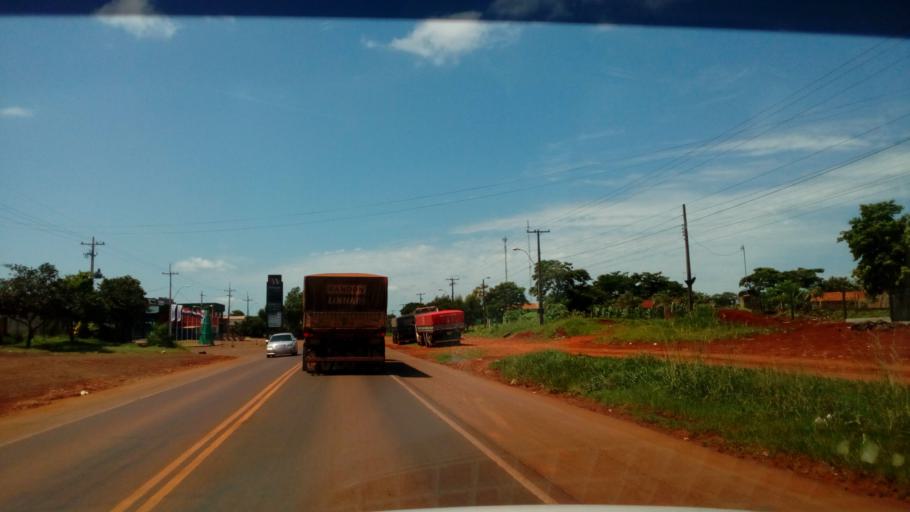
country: PY
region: Alto Parana
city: Colonia Yguazu
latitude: -25.4937
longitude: -54.8981
